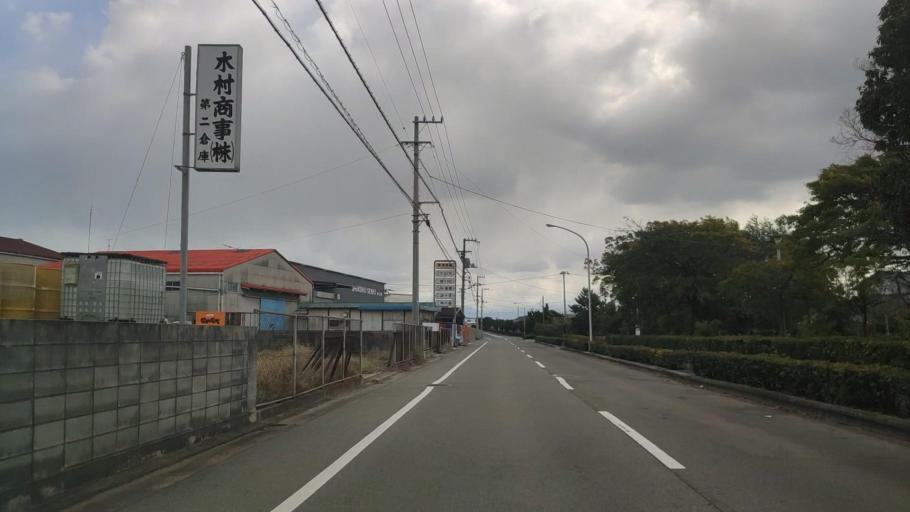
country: JP
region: Ehime
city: Saijo
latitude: 34.0543
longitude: 133.0221
